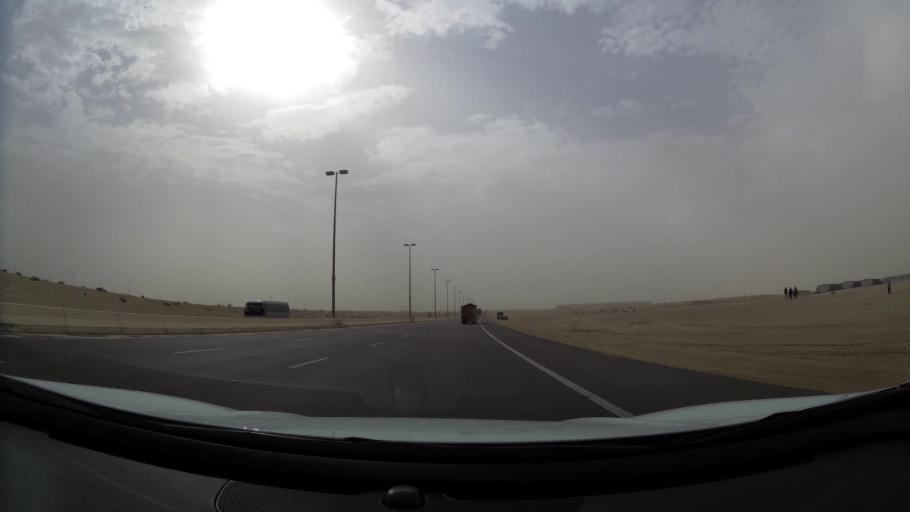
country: AE
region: Abu Dhabi
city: Abu Dhabi
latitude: 24.4721
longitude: 54.6705
